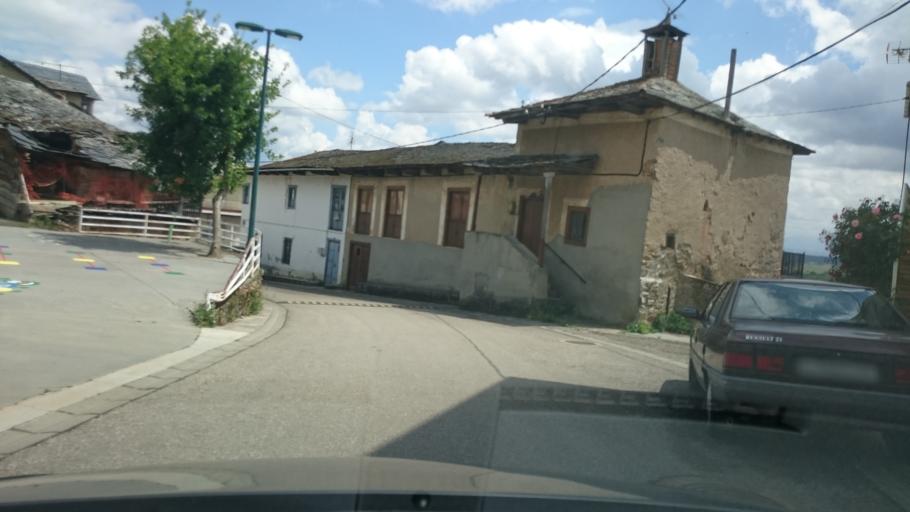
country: ES
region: Castille and Leon
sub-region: Provincia de Leon
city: Corullon
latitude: 42.5797
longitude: -6.8188
